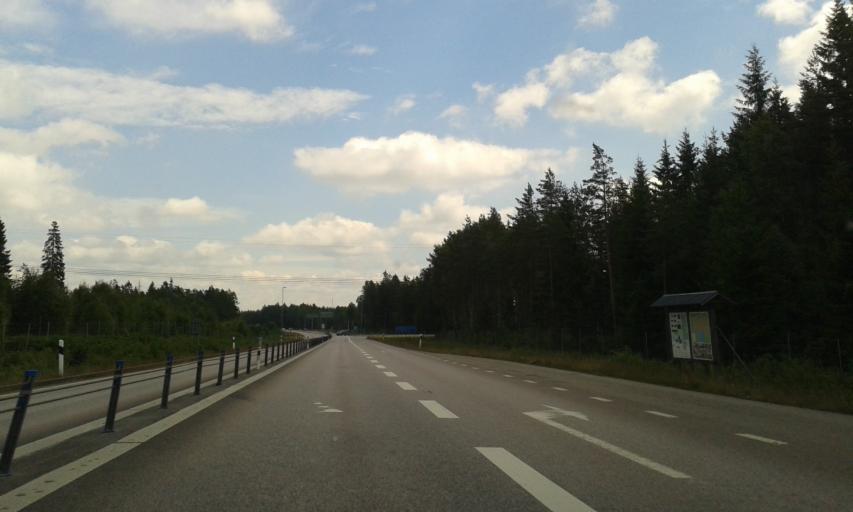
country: SE
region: Kronoberg
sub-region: Alvesta Kommun
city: Alvesta
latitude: 56.9147
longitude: 14.4953
